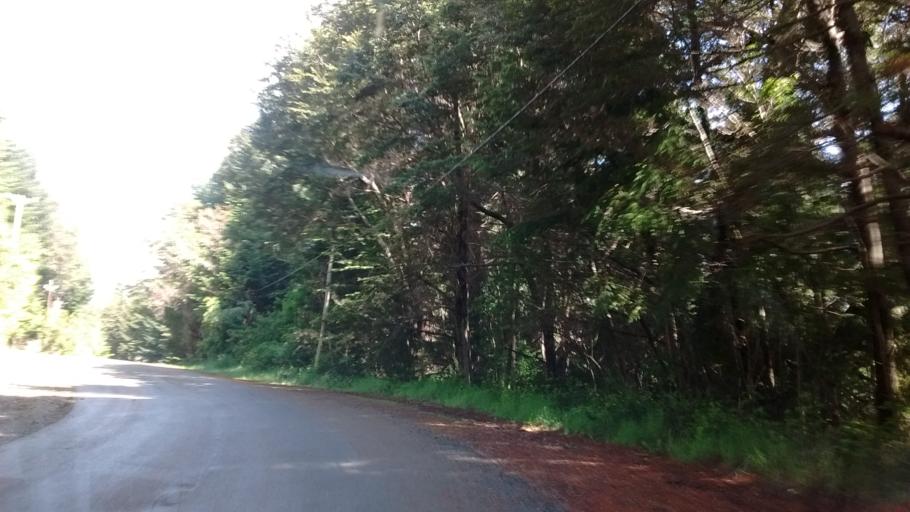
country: AR
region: Rio Negro
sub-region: Departamento de Bariloche
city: San Carlos de Bariloche
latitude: -41.0712
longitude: -71.5415
